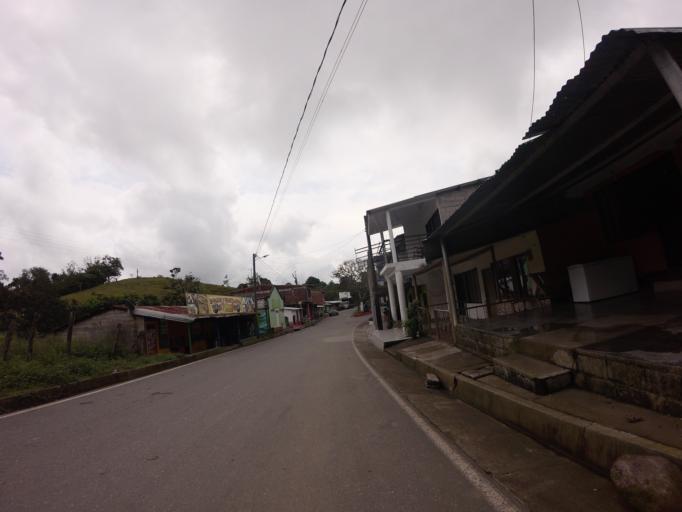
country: CO
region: Caldas
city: Victoria
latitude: 5.3225
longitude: -74.9416
